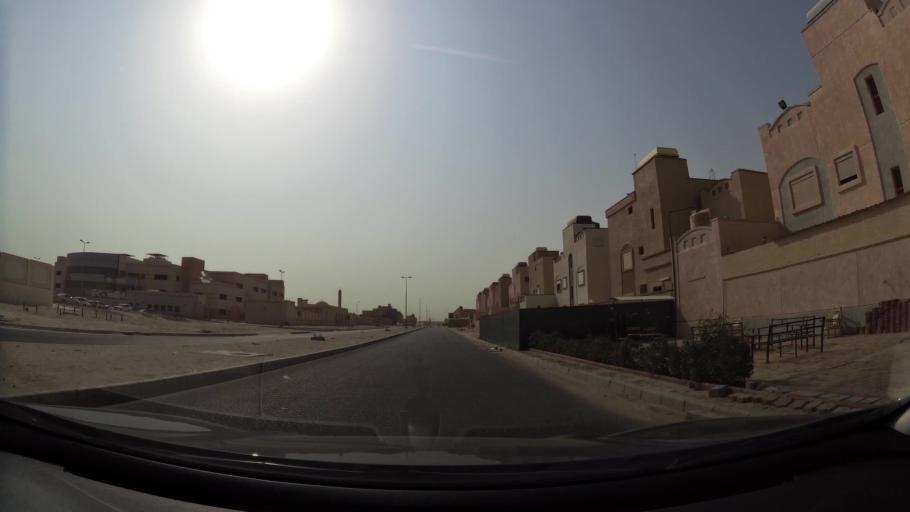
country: KW
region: Muhafazat al Jahra'
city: Al Jahra'
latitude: 29.3593
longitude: 47.7550
